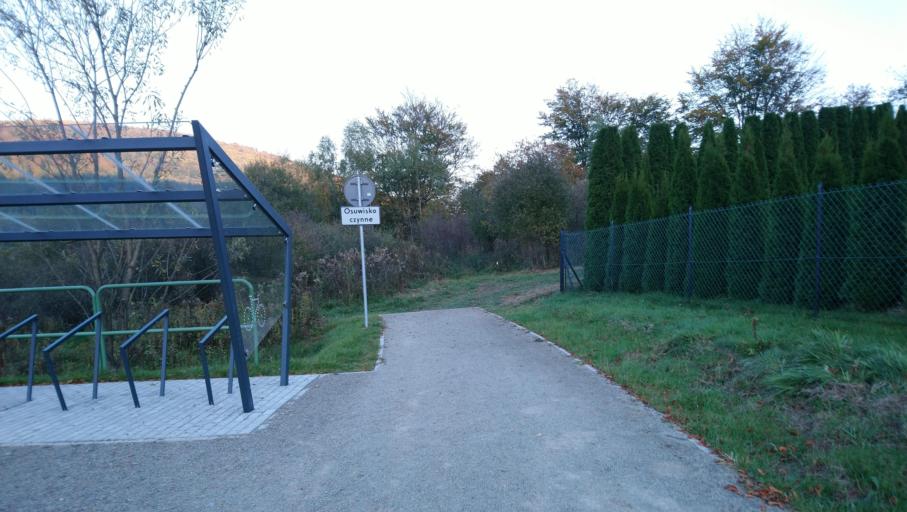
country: PL
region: Lesser Poland Voivodeship
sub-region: Powiat gorlicki
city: Uscie Gorlickie
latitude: 49.5357
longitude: 21.1042
